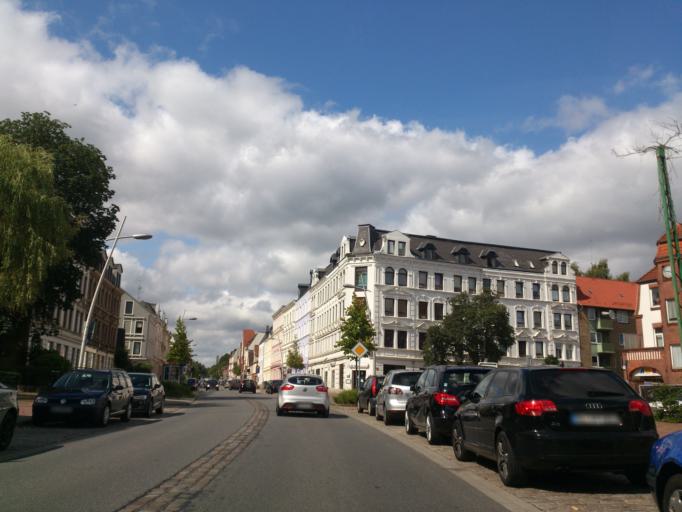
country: DE
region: Schleswig-Holstein
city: Flensburg
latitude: 54.8024
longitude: 9.4245
